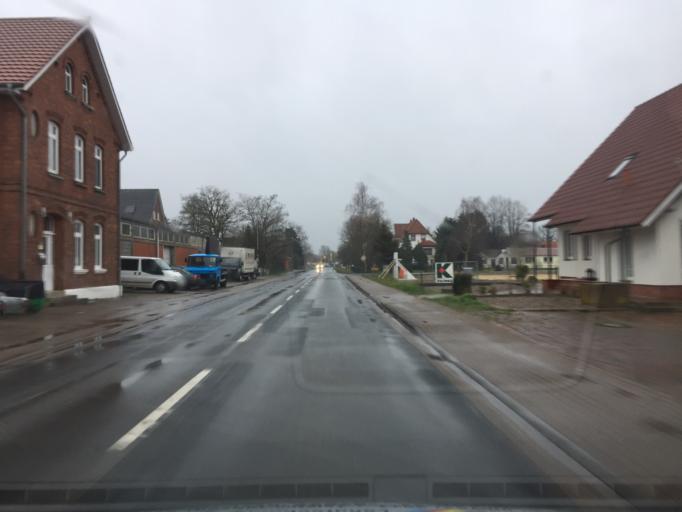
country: DE
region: Lower Saxony
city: Thedinghausen
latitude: 52.9532
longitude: 9.0098
